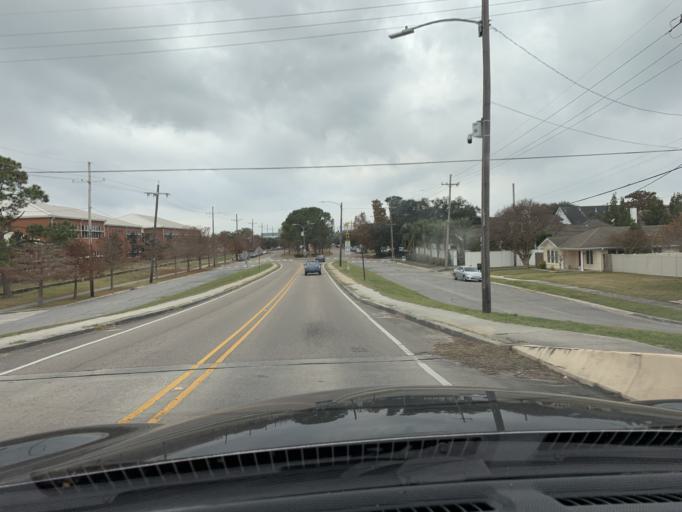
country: US
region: Louisiana
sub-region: Orleans Parish
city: New Orleans
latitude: 30.0040
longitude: -90.1002
